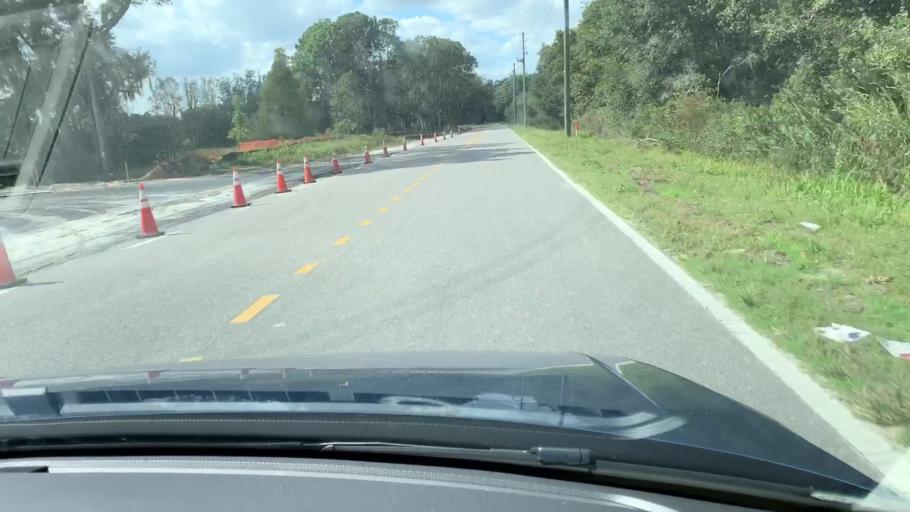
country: US
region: Florida
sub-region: Polk County
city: Winston
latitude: 28.0276
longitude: -82.0502
